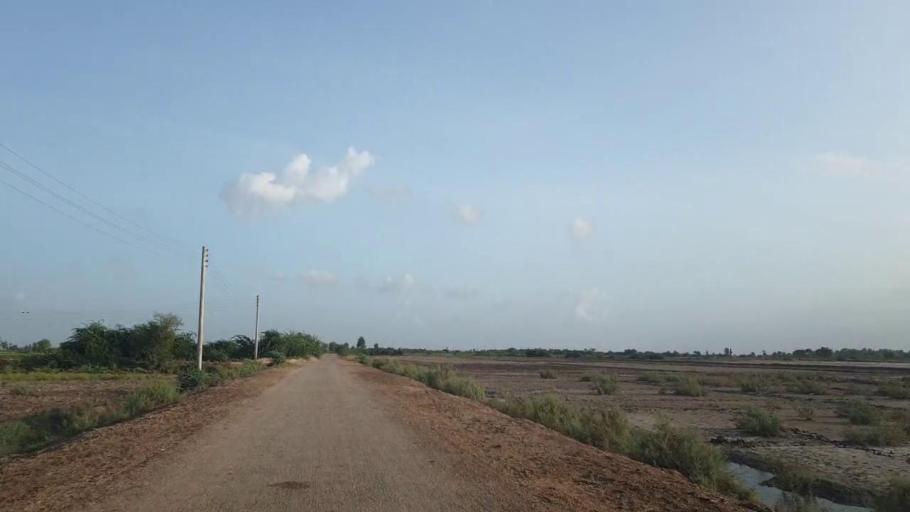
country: PK
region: Sindh
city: Kadhan
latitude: 24.6373
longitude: 69.1228
